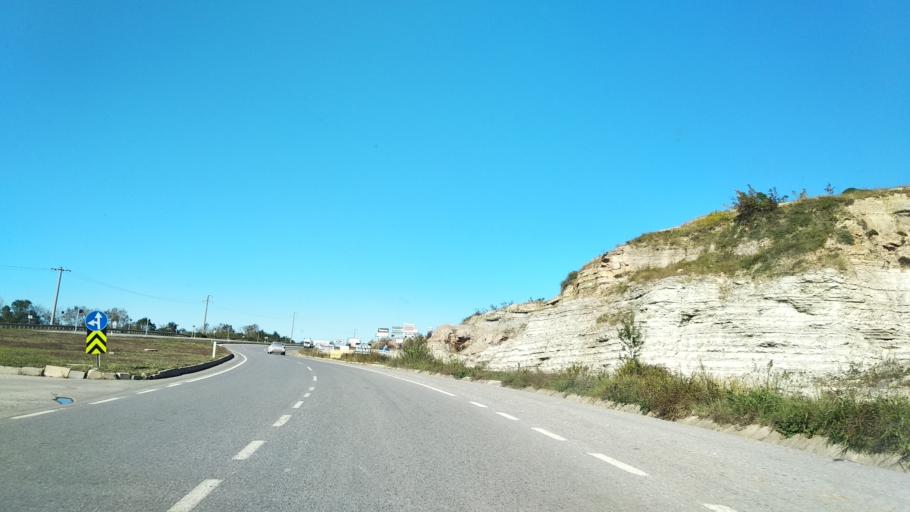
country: TR
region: Sakarya
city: Karasu
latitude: 41.0936
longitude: 30.6540
